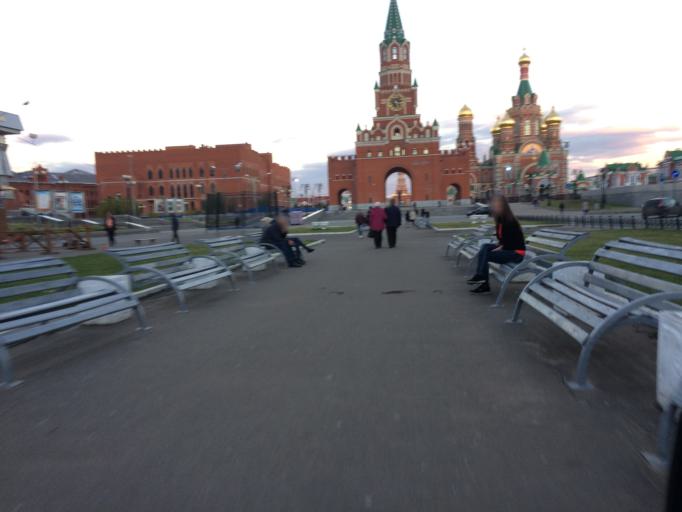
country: RU
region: Mariy-El
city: Yoshkar-Ola
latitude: 56.6342
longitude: 47.9006
